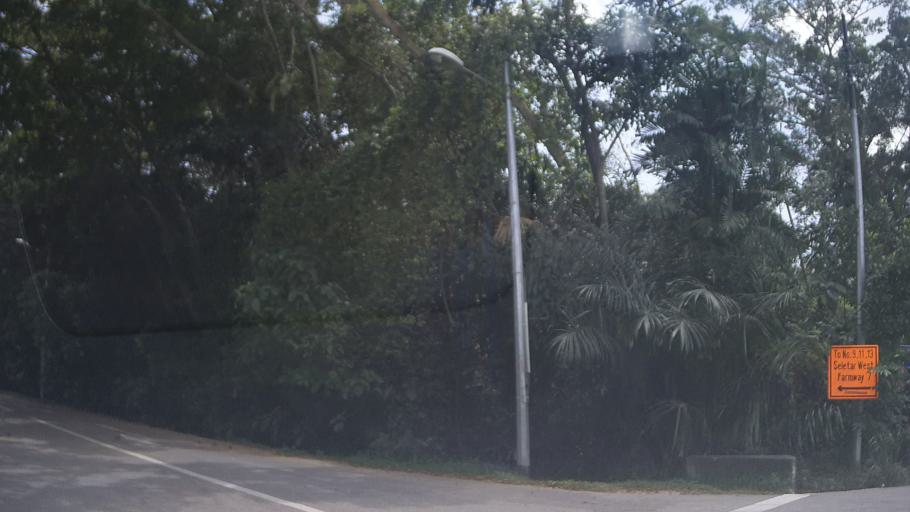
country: MY
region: Johor
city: Kampung Pasir Gudang Baru
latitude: 1.3976
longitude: 103.8649
